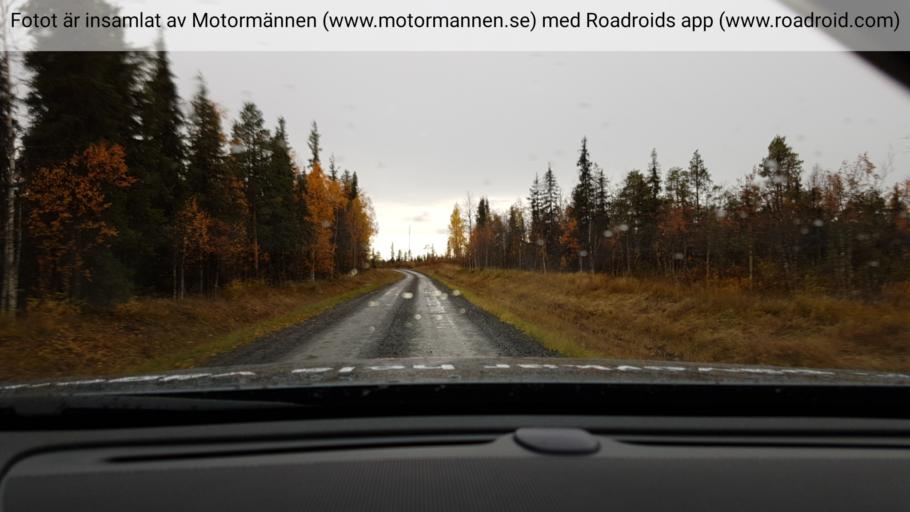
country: SE
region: Norrbotten
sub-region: Pajala Kommun
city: Pajala
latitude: 67.0697
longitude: 22.8154
